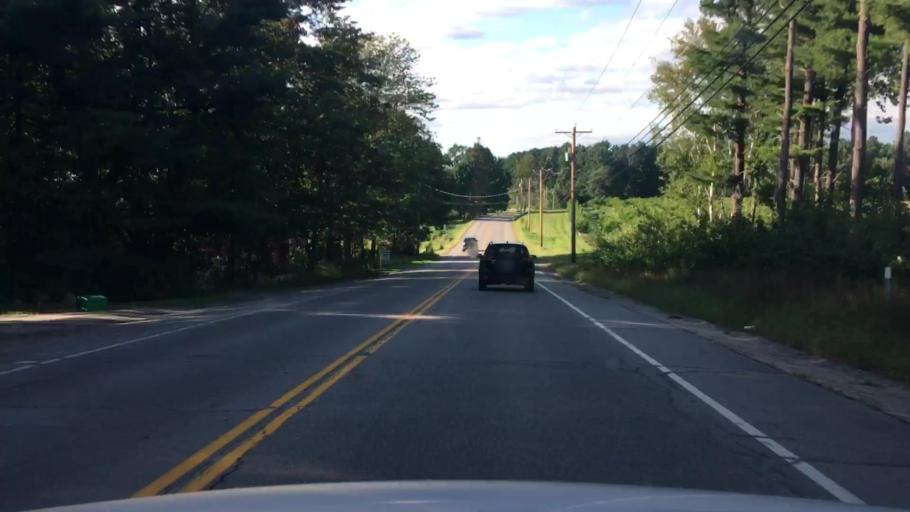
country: US
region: Maine
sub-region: York County
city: Eliot
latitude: 43.1577
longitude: -70.8416
